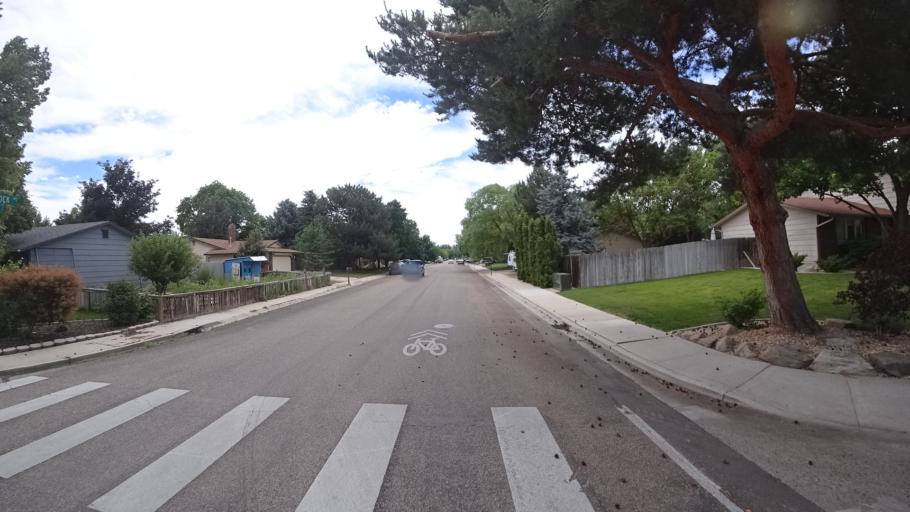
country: US
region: Idaho
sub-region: Ada County
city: Eagle
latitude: 43.6384
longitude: -116.3244
